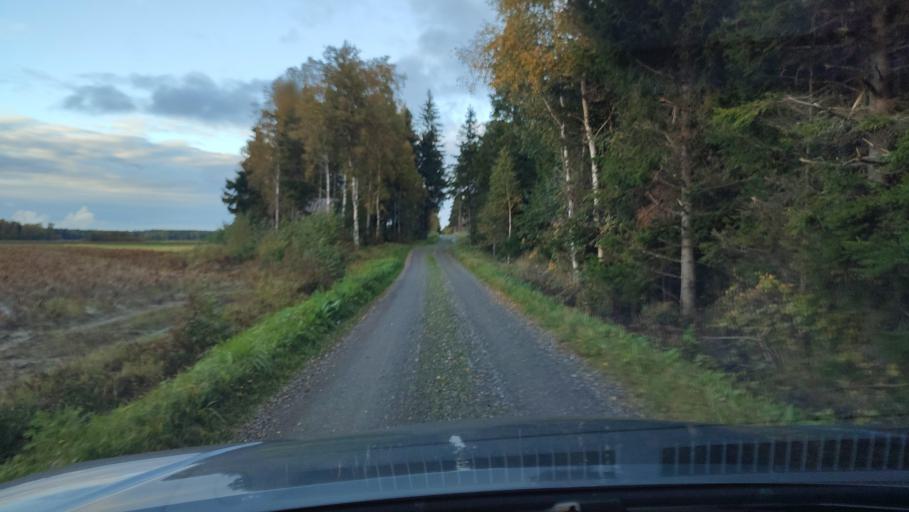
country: FI
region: Ostrobothnia
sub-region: Sydosterbotten
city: Kristinestad
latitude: 62.2461
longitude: 21.4529
